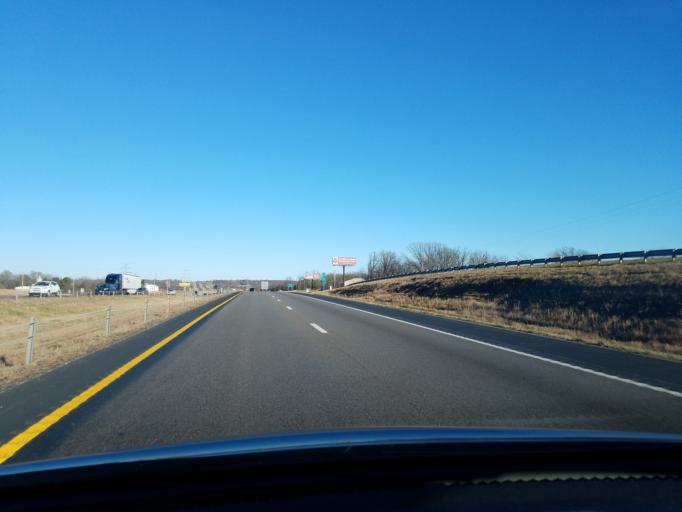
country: US
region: Missouri
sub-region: Phelps County
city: Saint James
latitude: 37.9861
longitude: -91.6713
